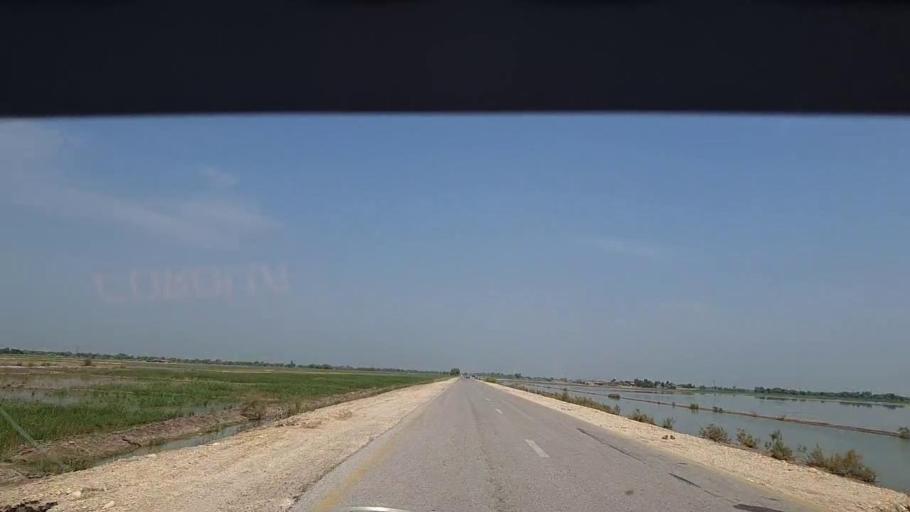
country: PK
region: Sindh
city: Rustam jo Goth
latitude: 28.0905
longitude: 68.7993
